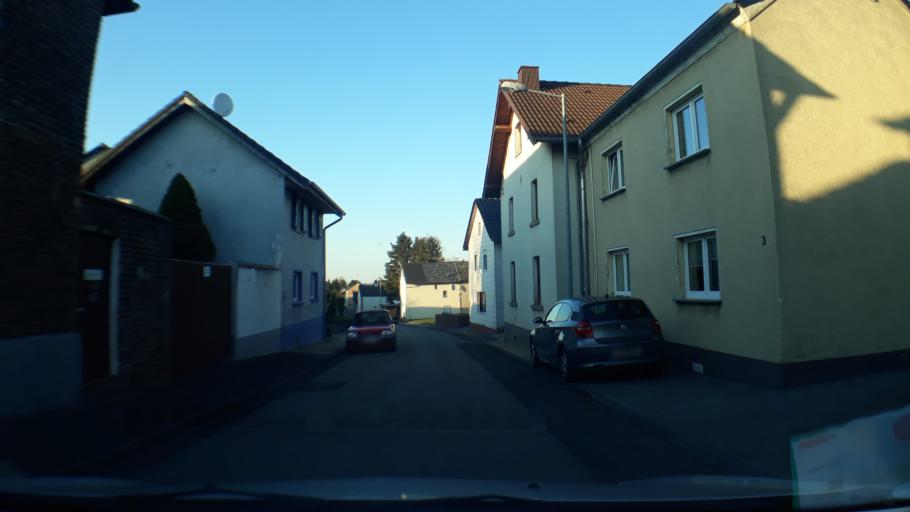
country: DE
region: North Rhine-Westphalia
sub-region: Regierungsbezirk Koln
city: Kall
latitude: 50.5684
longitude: 6.5992
